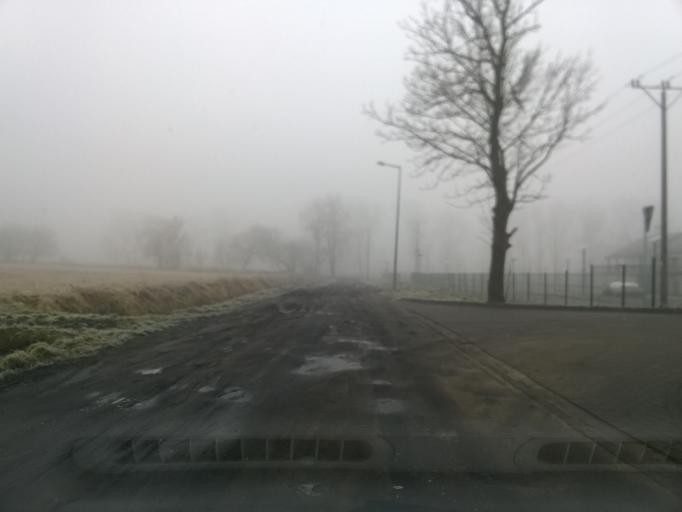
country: PL
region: Kujawsko-Pomorskie
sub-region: Powiat nakielski
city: Naklo nad Notecia
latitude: 53.1315
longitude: 17.6054
